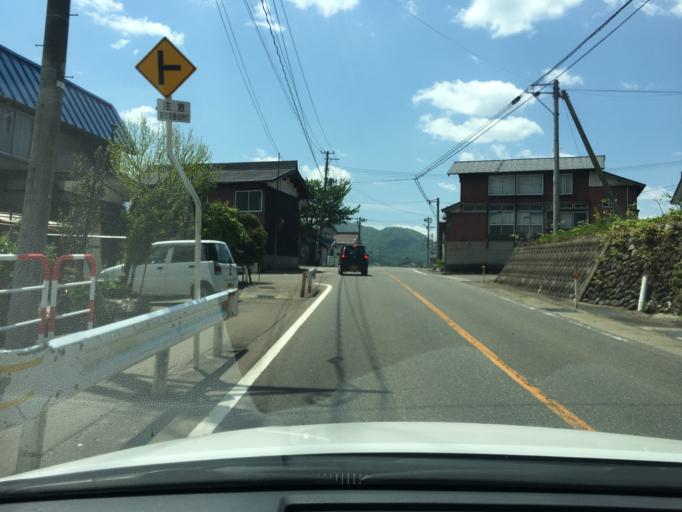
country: JP
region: Niigata
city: Tochio-honcho
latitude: 37.3300
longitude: 139.0267
